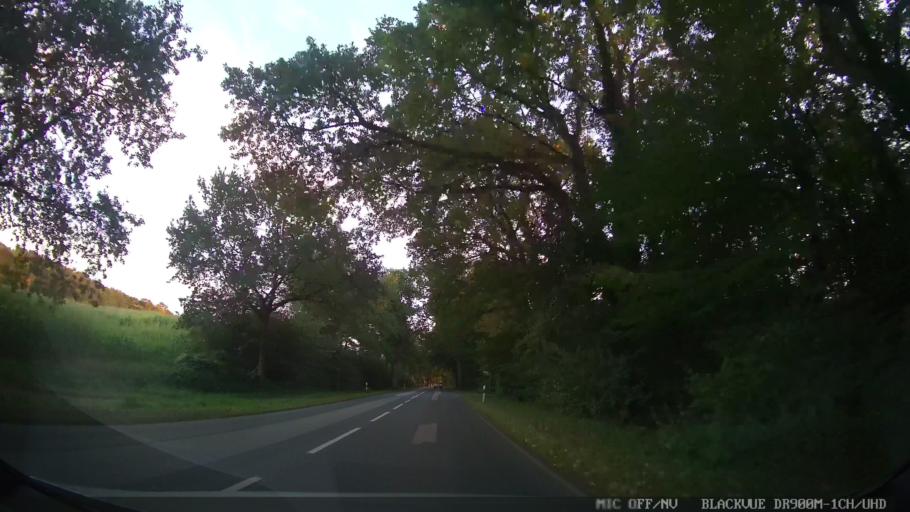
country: DE
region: Schleswig-Holstein
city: Susel
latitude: 54.0205
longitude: 10.6848
